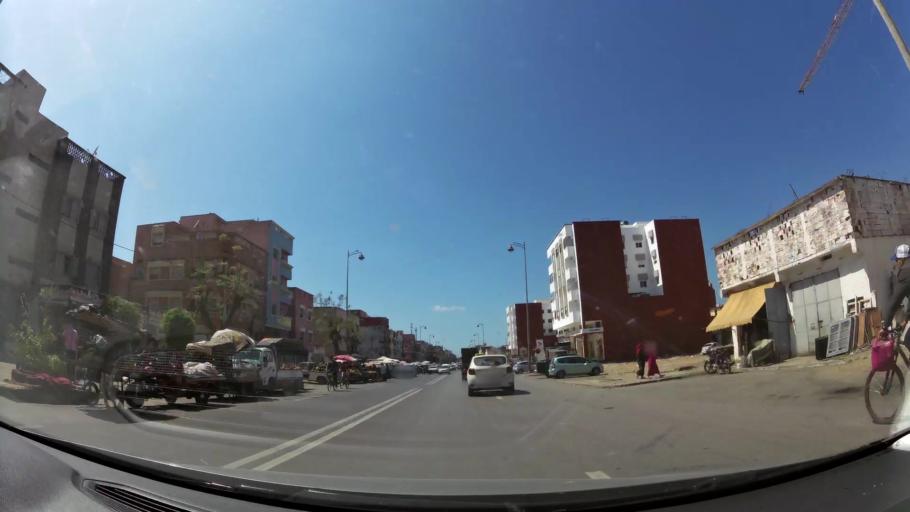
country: MA
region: Gharb-Chrarda-Beni Hssen
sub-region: Kenitra Province
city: Kenitra
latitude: 34.2432
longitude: -6.5502
